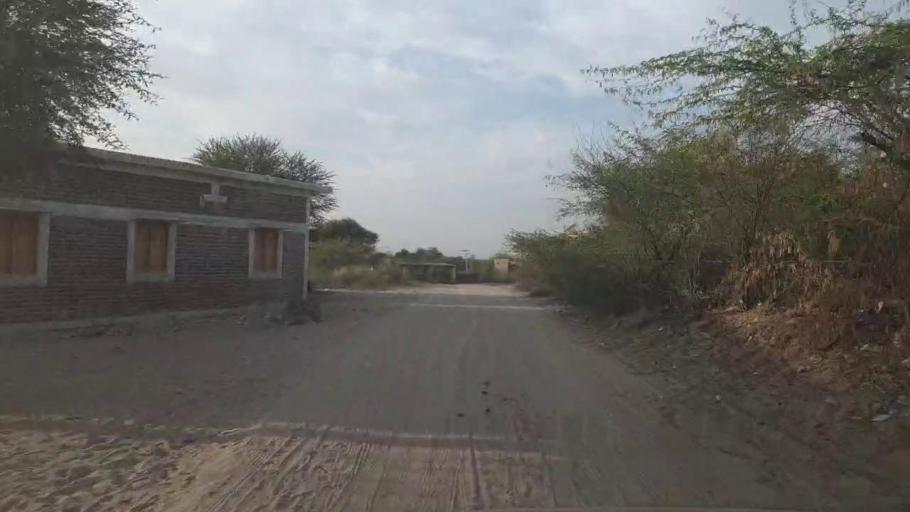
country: PK
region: Sindh
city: Nabisar
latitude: 25.1489
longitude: 69.6702
